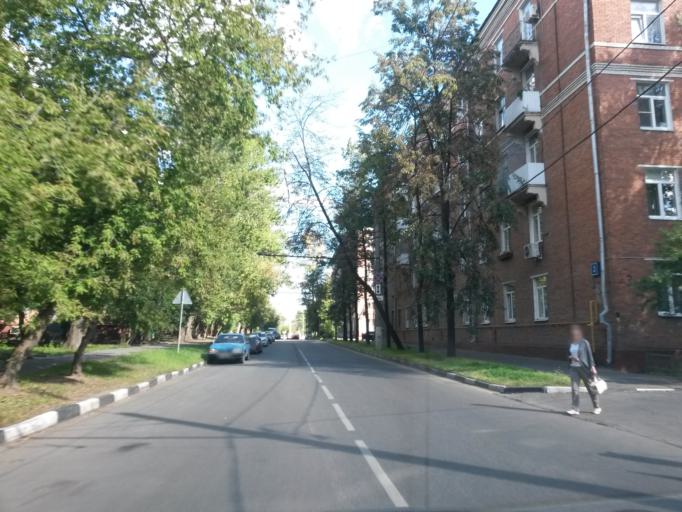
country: RU
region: Moscow
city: Kotlovka
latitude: 55.6670
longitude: 37.6176
